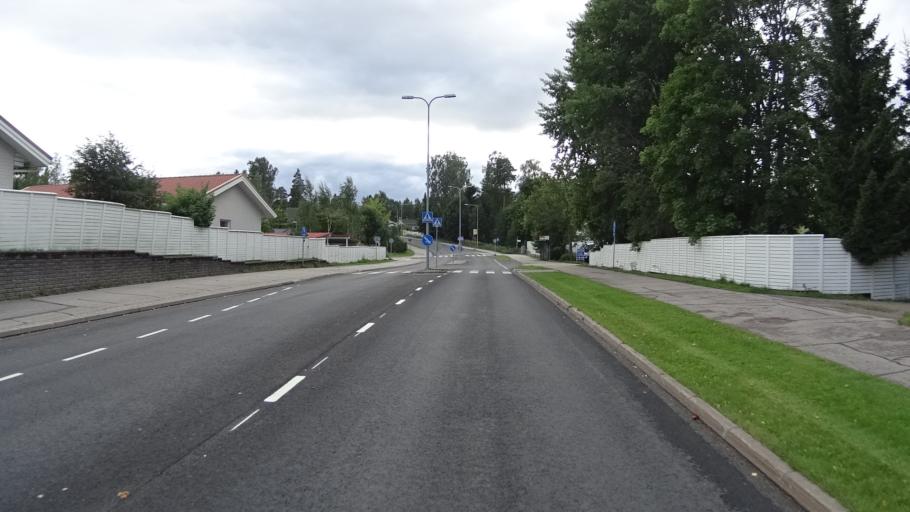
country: FI
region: Uusimaa
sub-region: Helsinki
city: Kauniainen
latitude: 60.2223
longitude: 24.7432
